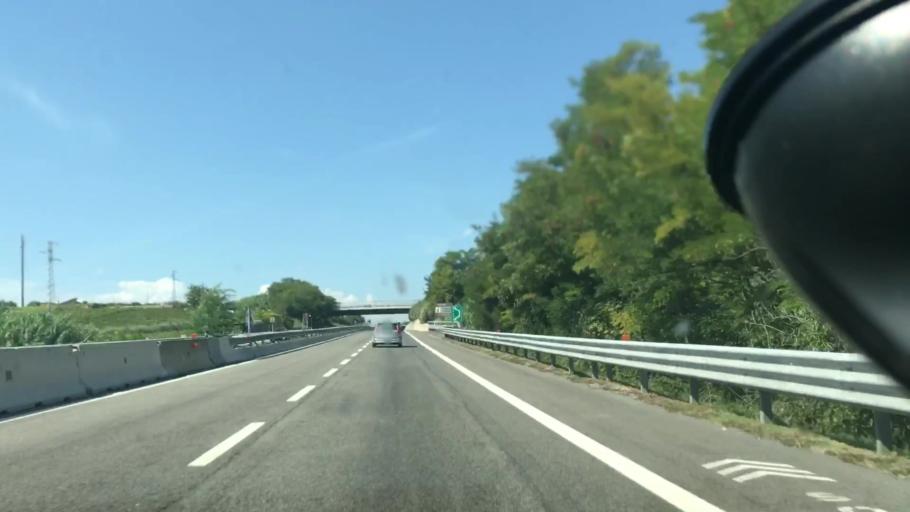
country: IT
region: Abruzzo
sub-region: Provincia di Chieti
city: Tollo
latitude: 42.3613
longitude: 14.3354
